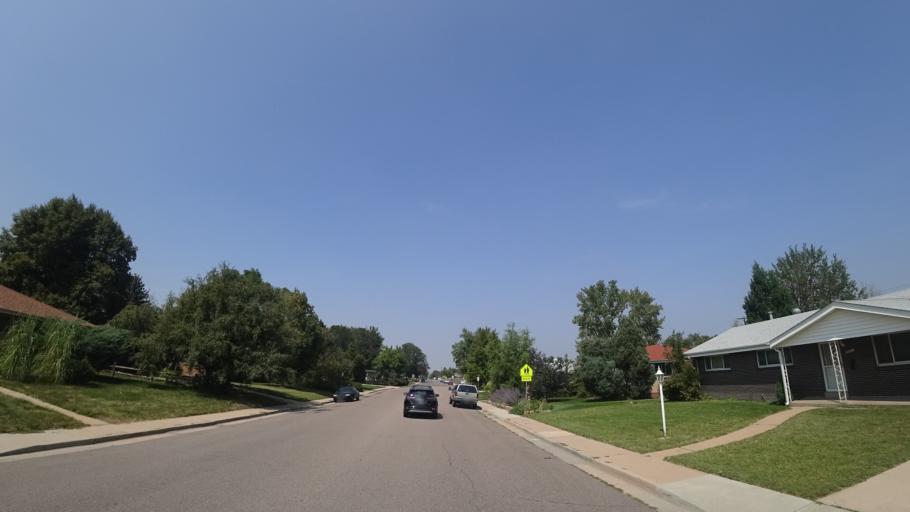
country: US
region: Colorado
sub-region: Arapahoe County
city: Englewood
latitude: 39.6248
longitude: -104.9927
